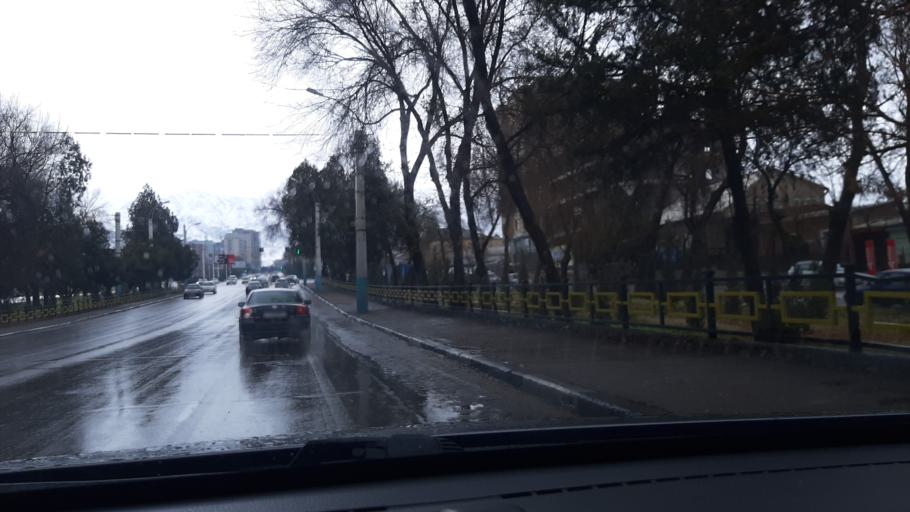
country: TJ
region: Viloyati Sughd
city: Khujand
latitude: 40.2932
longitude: 69.6185
